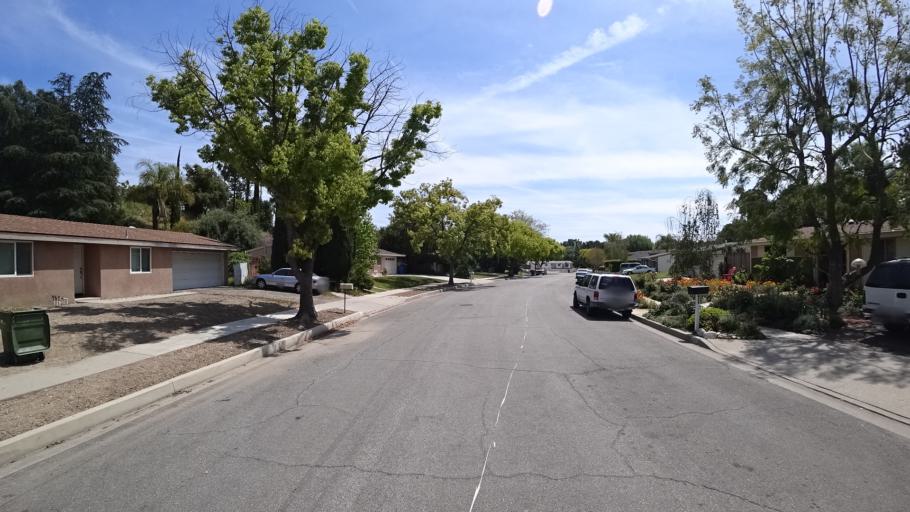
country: US
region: California
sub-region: Ventura County
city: Thousand Oaks
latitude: 34.1937
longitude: -118.8638
